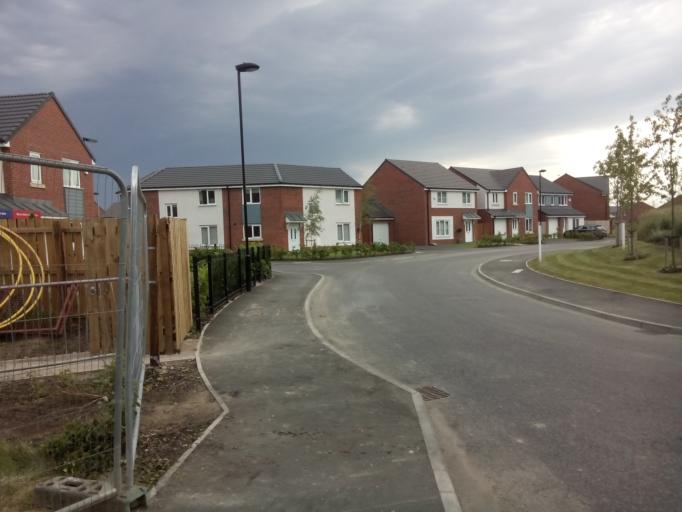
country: GB
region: England
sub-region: Northumberland
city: Backworth
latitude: 55.0235
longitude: -1.5362
